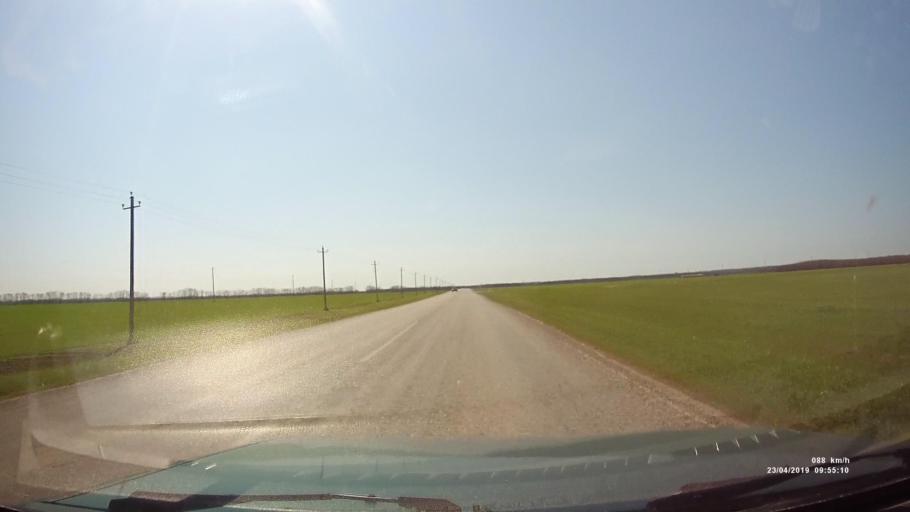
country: RU
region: Rostov
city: Orlovskiy
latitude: 46.8122
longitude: 42.0607
